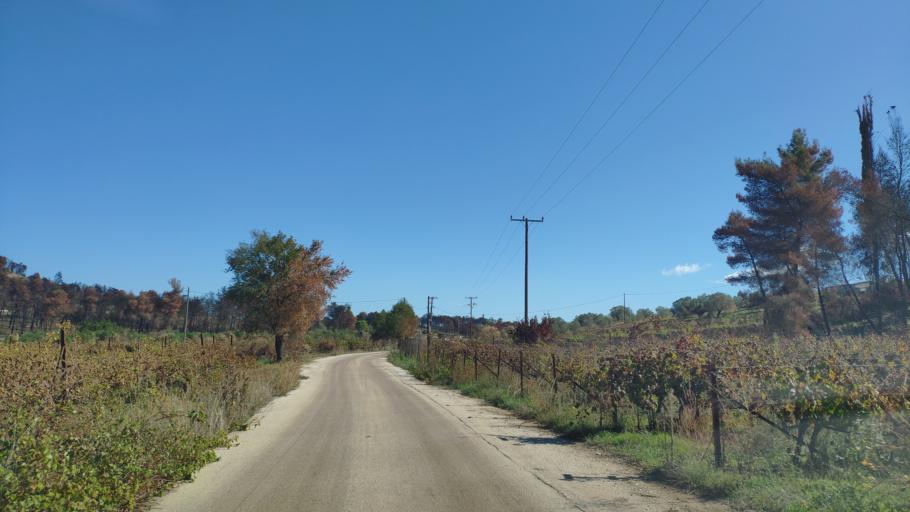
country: GR
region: Peloponnese
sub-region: Nomos Korinthias
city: Athikia
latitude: 37.8449
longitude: 22.9439
